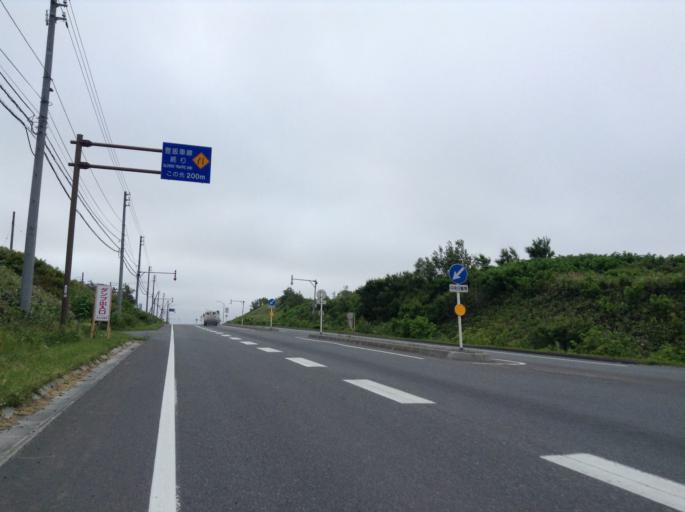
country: JP
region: Hokkaido
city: Wakkanai
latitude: 45.3750
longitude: 141.7138
